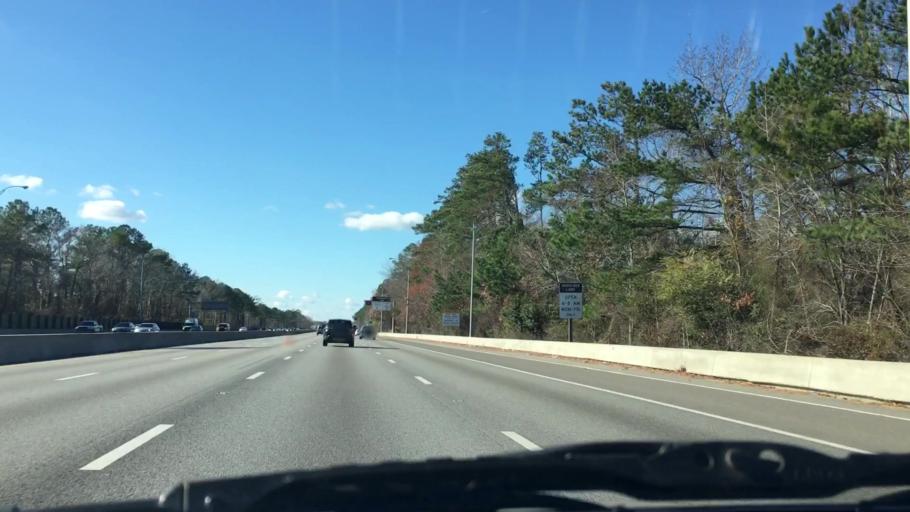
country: US
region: Virginia
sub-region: City of Virginia Beach
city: Virginia Beach
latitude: 36.8363
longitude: -76.1049
